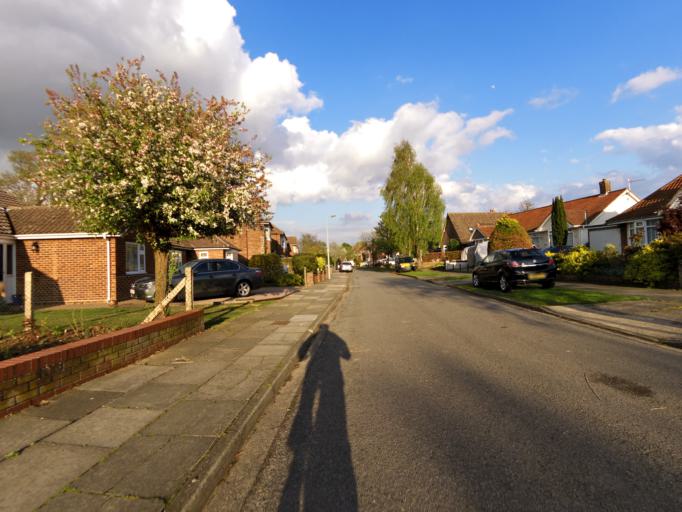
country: GB
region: England
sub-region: Suffolk
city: Ipswich
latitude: 52.0731
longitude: 1.1674
